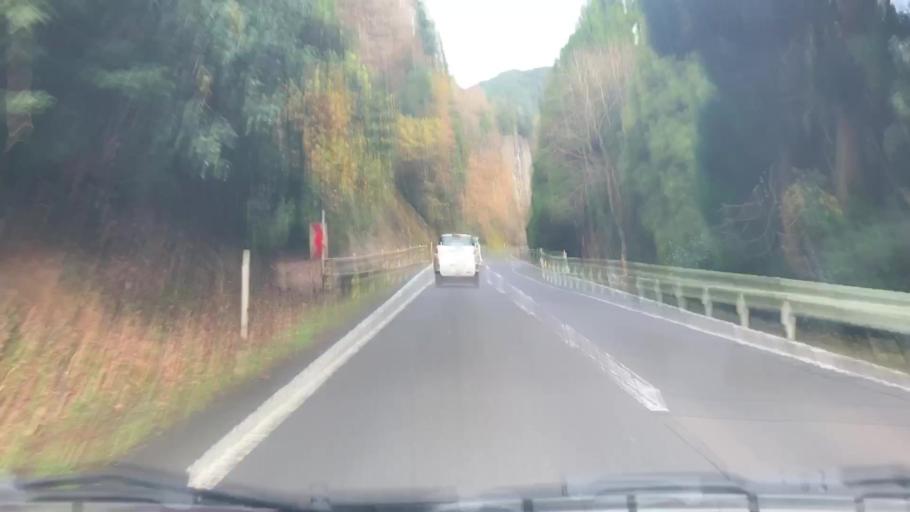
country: JP
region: Saga Prefecture
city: Imaricho-ko
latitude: 33.3317
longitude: 129.9701
